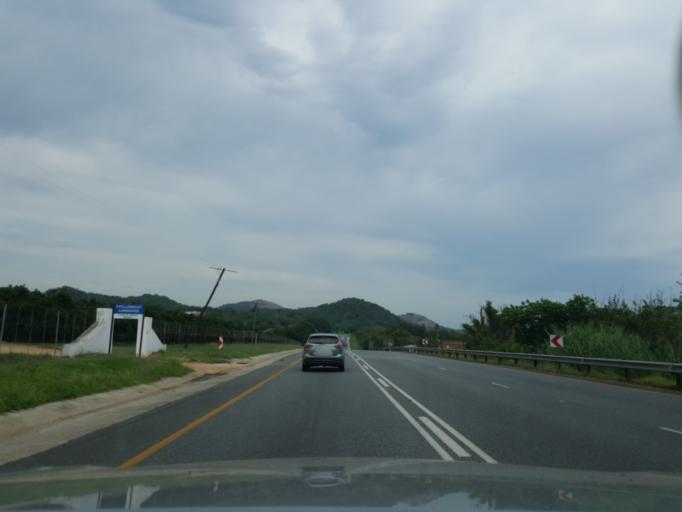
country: ZA
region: Mpumalanga
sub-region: Ehlanzeni District
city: Nelspruit
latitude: -25.4732
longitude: 31.1012
